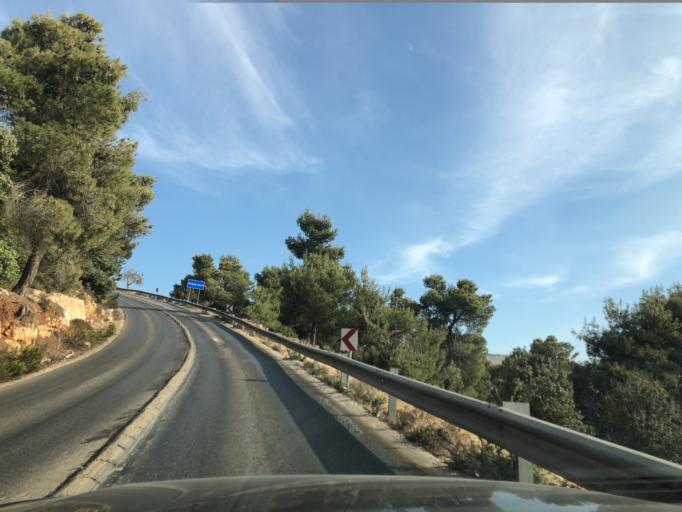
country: JO
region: Irbid
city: `Ayn Jannah
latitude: 32.3213
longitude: 35.7611
